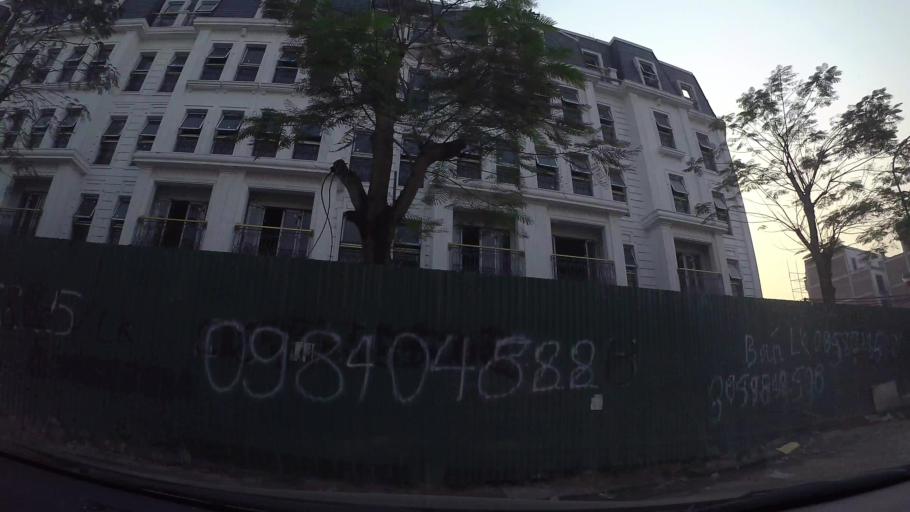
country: VN
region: Ha Noi
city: Thanh Xuan
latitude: 20.9786
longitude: 105.8146
